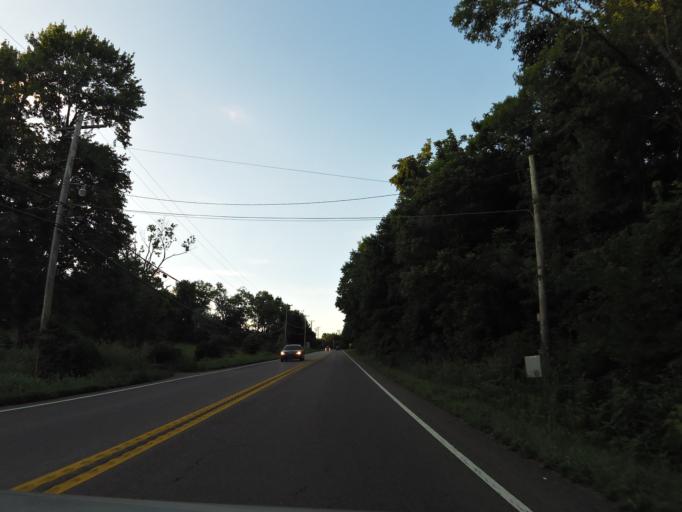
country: US
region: Tennessee
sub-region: Loudon County
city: Lenoir City
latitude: 35.8504
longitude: -84.2258
